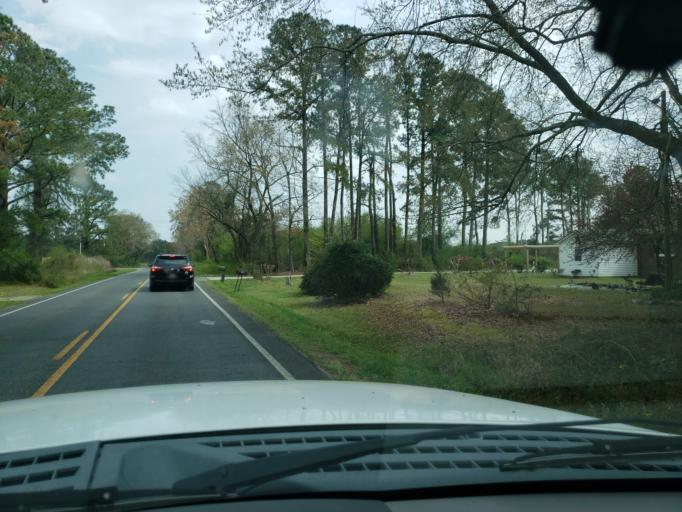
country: US
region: North Carolina
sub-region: Duplin County
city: Beulaville
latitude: 34.7745
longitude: -77.8134
